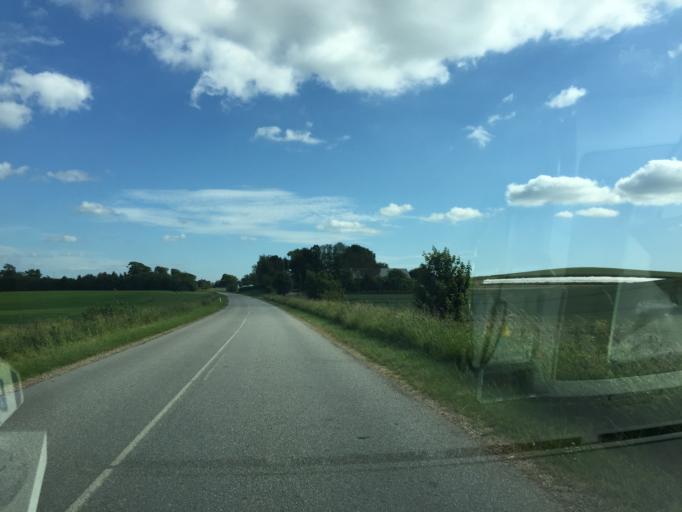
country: DK
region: South Denmark
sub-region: Aabenraa Kommune
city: Lojt Kirkeby
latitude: 55.1631
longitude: 9.4642
